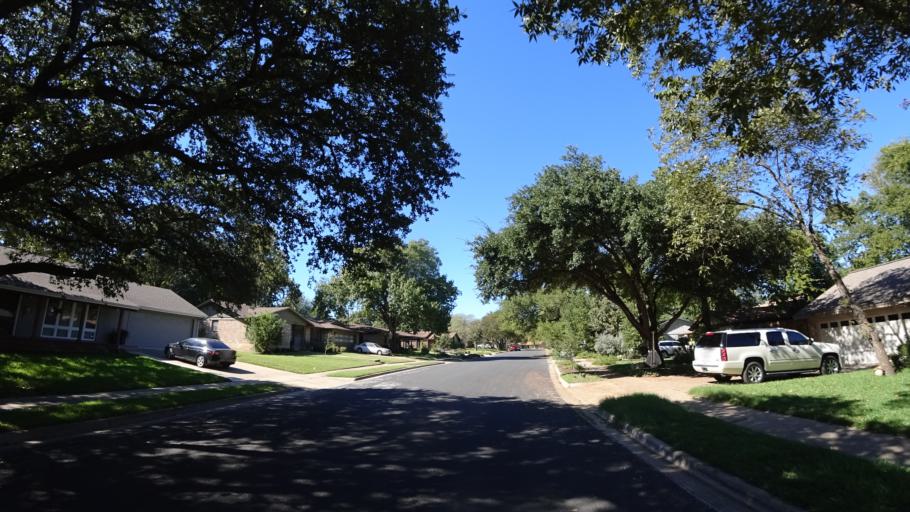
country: US
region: Texas
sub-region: Travis County
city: West Lake Hills
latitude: 30.3372
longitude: -97.7507
